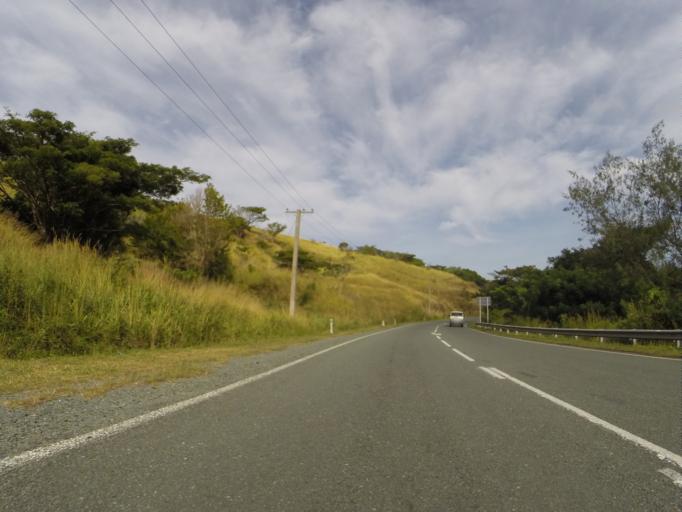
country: FJ
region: Western
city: Nadi
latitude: -18.1740
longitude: 177.5483
